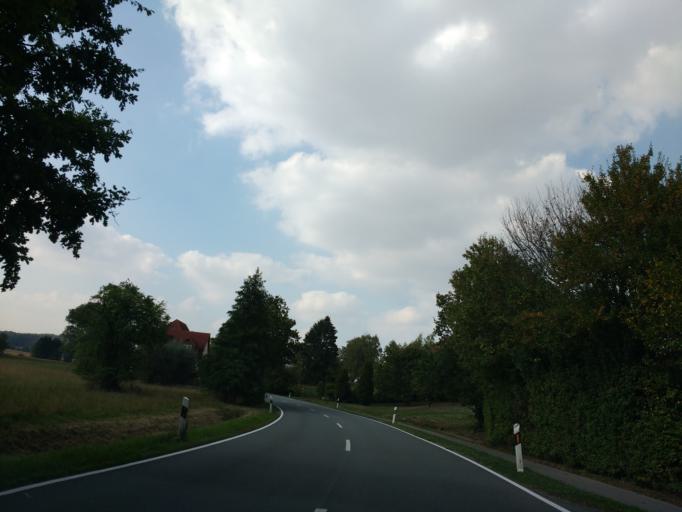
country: DE
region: North Rhine-Westphalia
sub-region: Regierungsbezirk Detmold
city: Bad Meinberg
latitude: 51.9334
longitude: 9.0266
